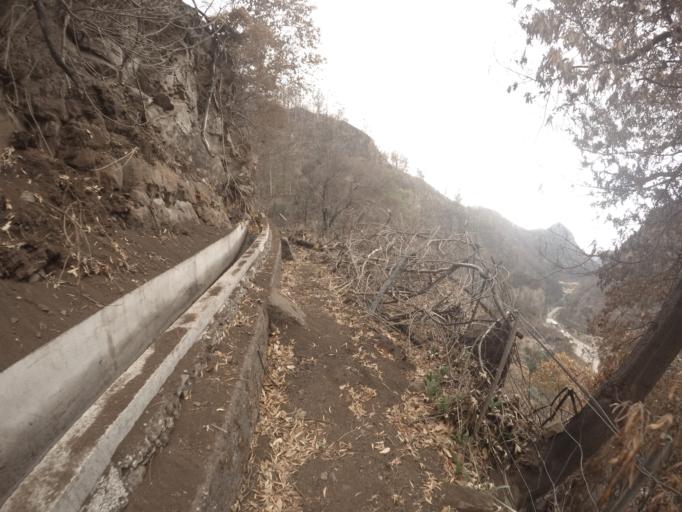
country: PT
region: Madeira
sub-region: Funchal
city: Nossa Senhora do Monte
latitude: 32.6882
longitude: -16.9145
